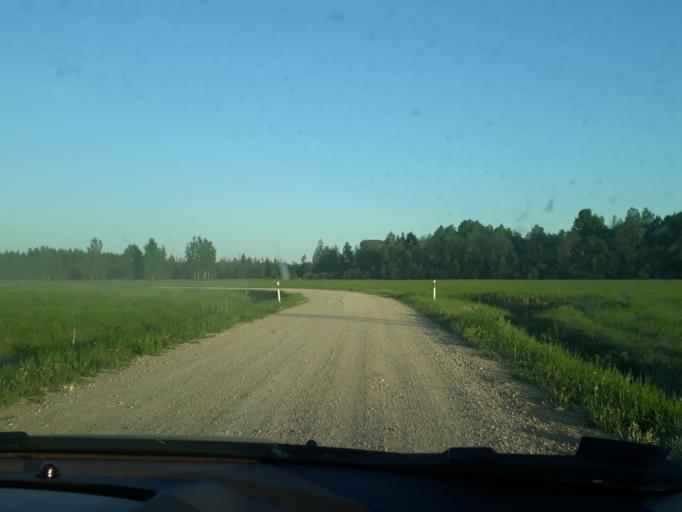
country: EE
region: Paernumaa
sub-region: Tootsi vald
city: Tootsi
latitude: 58.5819
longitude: 24.9071
